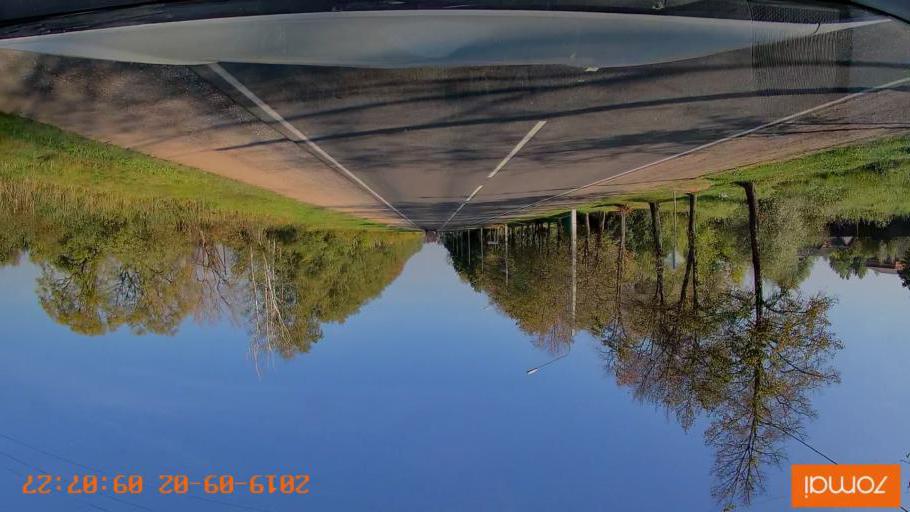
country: RU
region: Kaluga
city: Myatlevo
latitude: 54.8957
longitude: 35.6576
